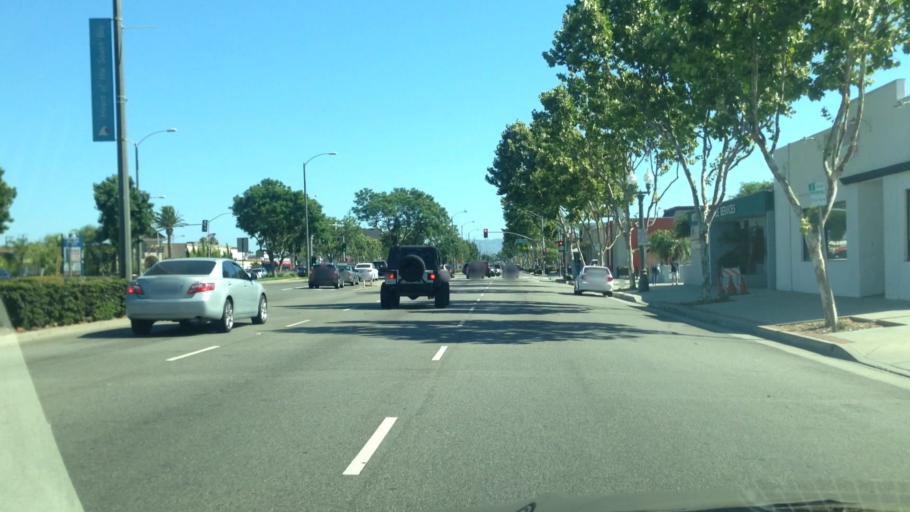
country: US
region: California
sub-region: Los Angeles County
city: Lawndale
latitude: 33.8959
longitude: -118.3528
